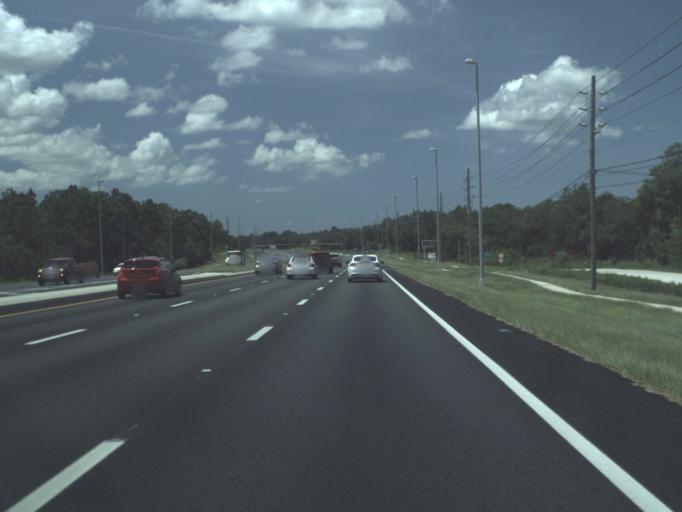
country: US
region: Florida
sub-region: Hernando County
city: High Point
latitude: 28.5336
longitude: -82.5290
